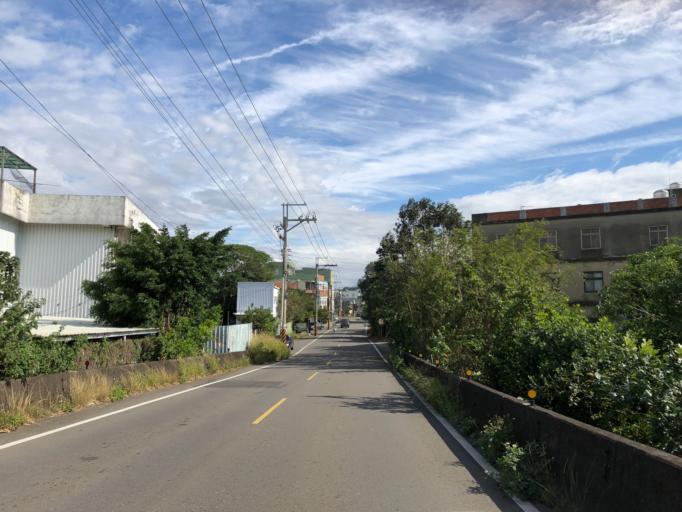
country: TW
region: Taiwan
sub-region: Hsinchu
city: Zhubei
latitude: 24.7914
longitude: 121.0604
